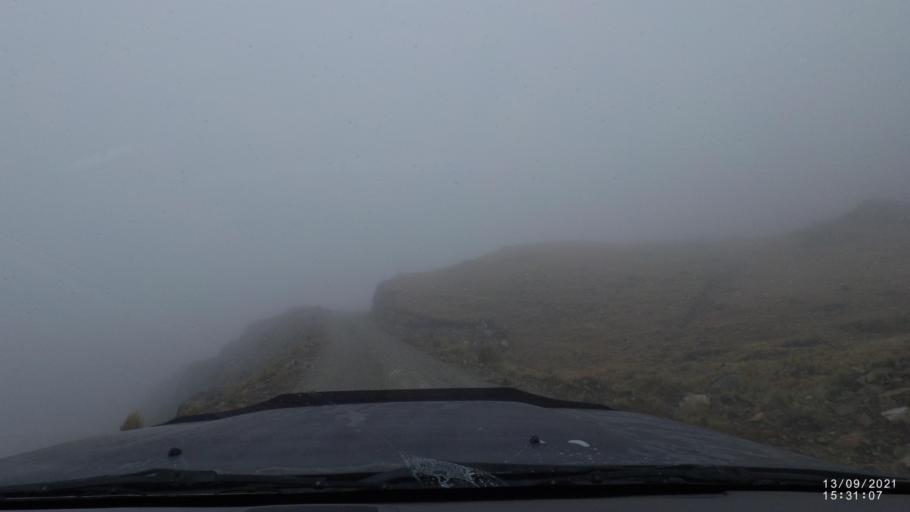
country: BO
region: Cochabamba
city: Colomi
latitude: -17.3428
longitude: -65.7525
